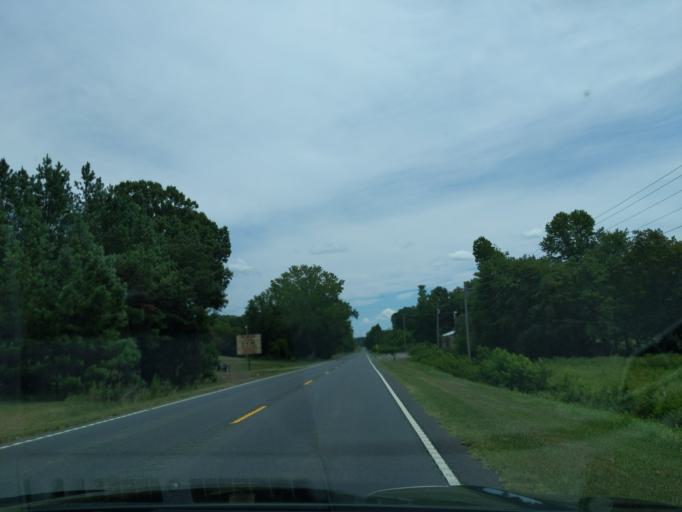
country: US
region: North Carolina
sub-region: Rowan County
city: Rockwell
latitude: 35.4640
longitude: -80.3017
